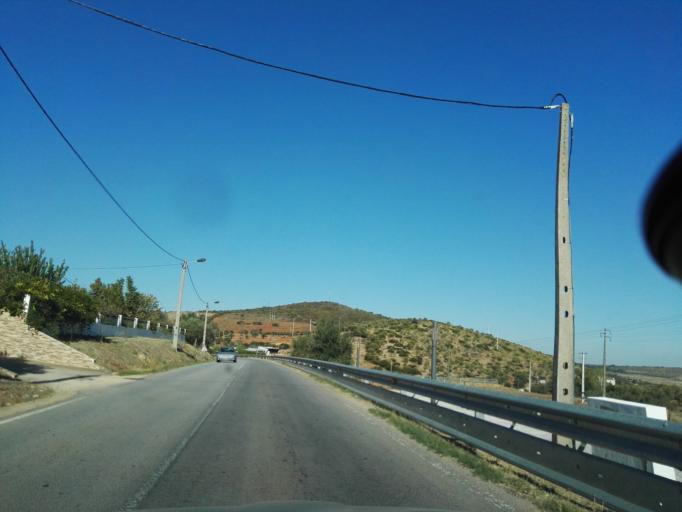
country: PT
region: Portalegre
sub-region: Elvas
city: Elvas
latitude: 38.8927
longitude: -7.1710
